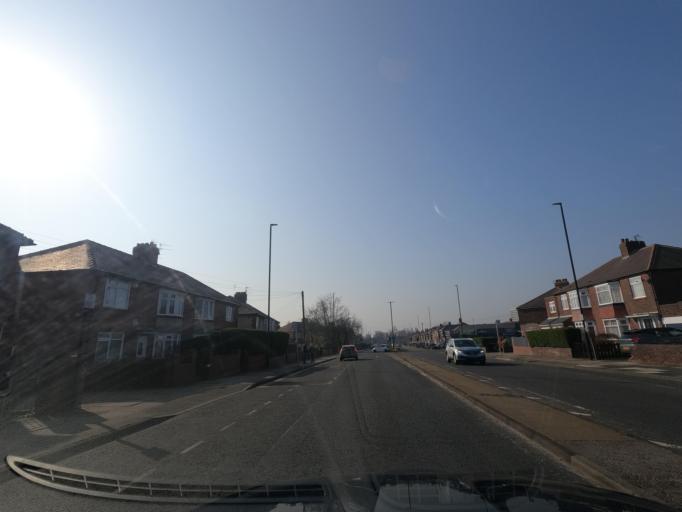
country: GB
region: England
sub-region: Newcastle upon Tyne
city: Gosforth
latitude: 55.0003
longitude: -1.5800
